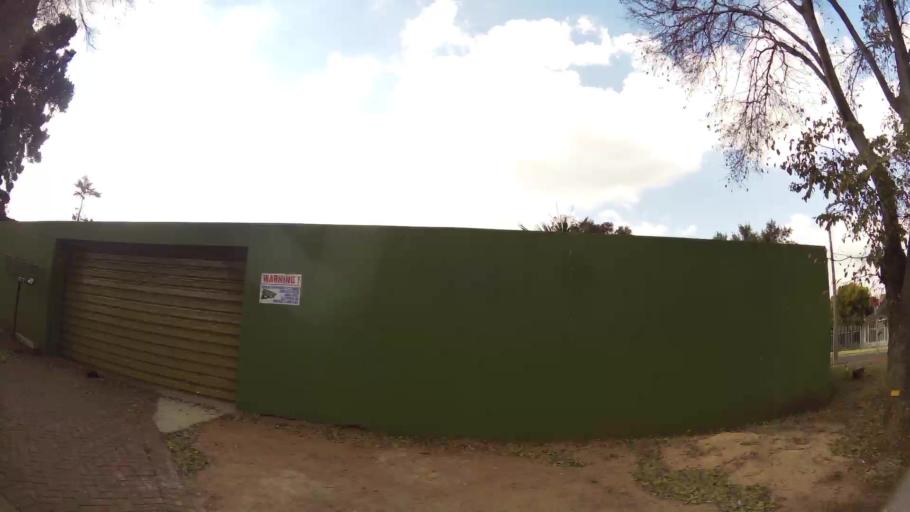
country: ZA
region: Mpumalanga
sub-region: Nkangala District Municipality
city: Delmas
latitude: -26.1408
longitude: 28.6703
